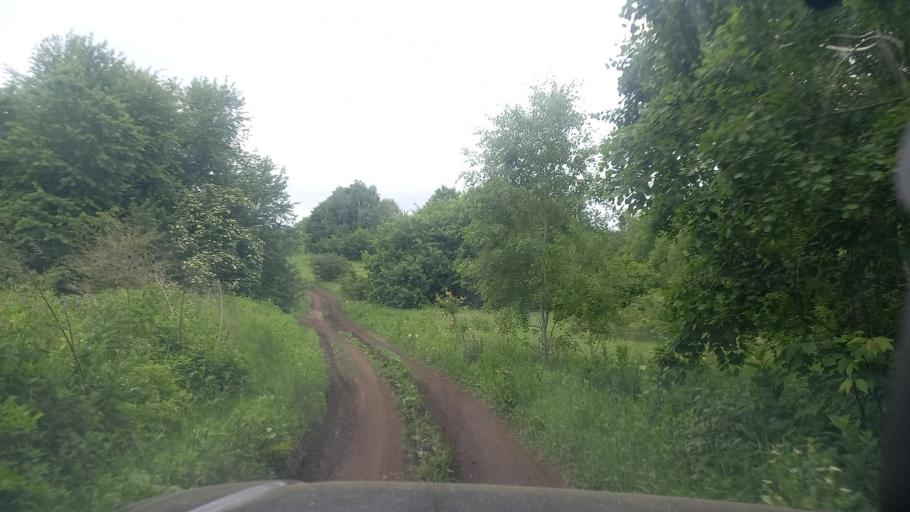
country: RU
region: Karachayevo-Cherkesiya
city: Pregradnaya
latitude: 44.0362
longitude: 41.3176
